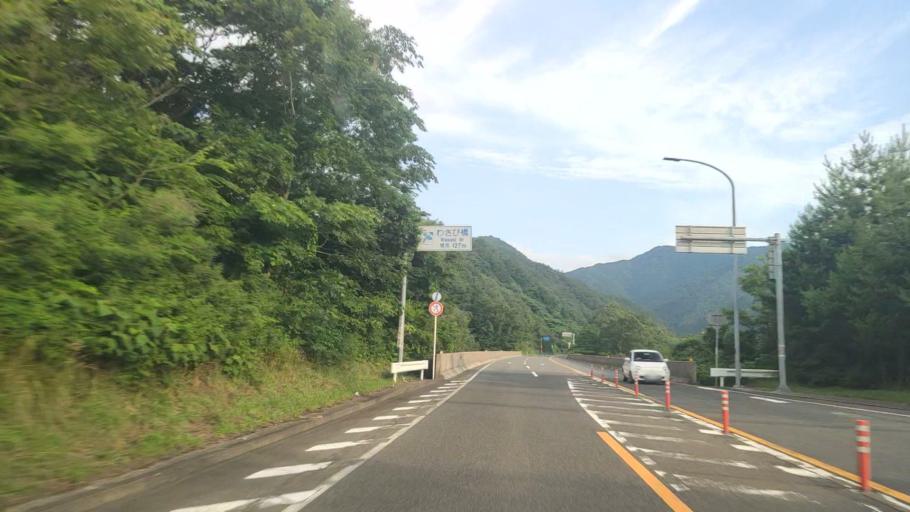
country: JP
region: Tottori
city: Kurayoshi
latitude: 35.3276
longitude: 133.7555
